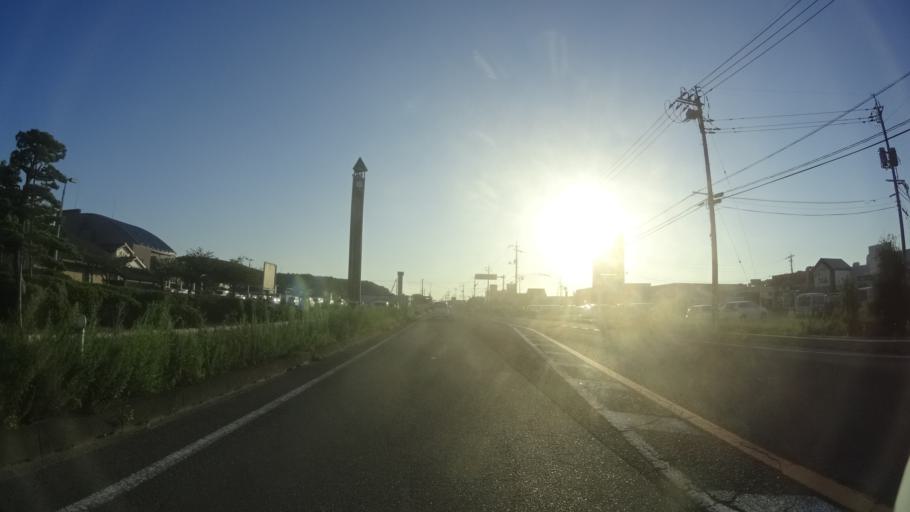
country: JP
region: Tottori
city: Yonago
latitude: 35.4534
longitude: 133.4191
